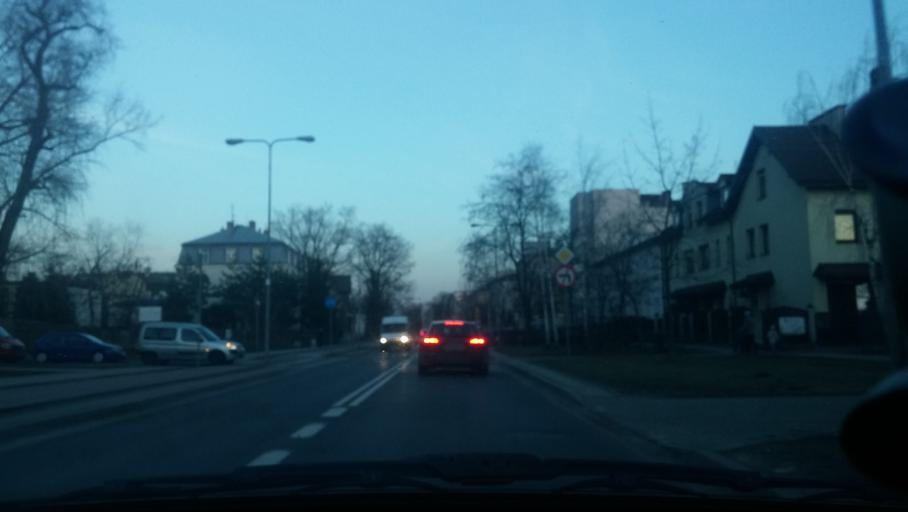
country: PL
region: Masovian Voivodeship
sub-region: Warszawa
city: Praga Poludnie
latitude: 52.2458
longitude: 21.1067
